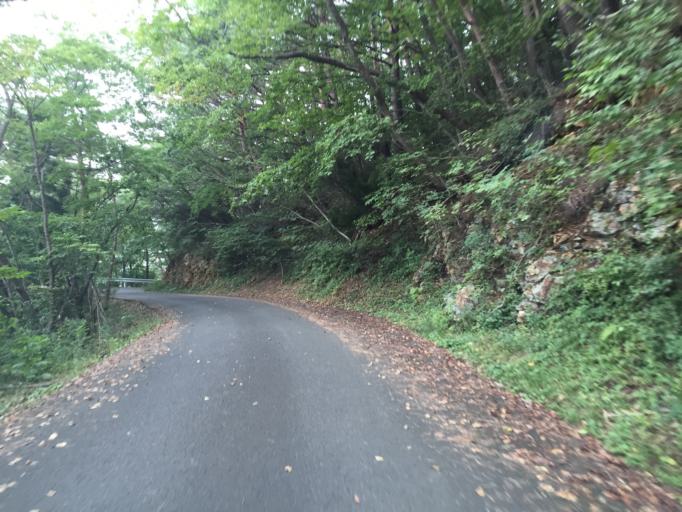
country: JP
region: Fukushima
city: Fukushima-shi
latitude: 37.7743
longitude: 140.4703
